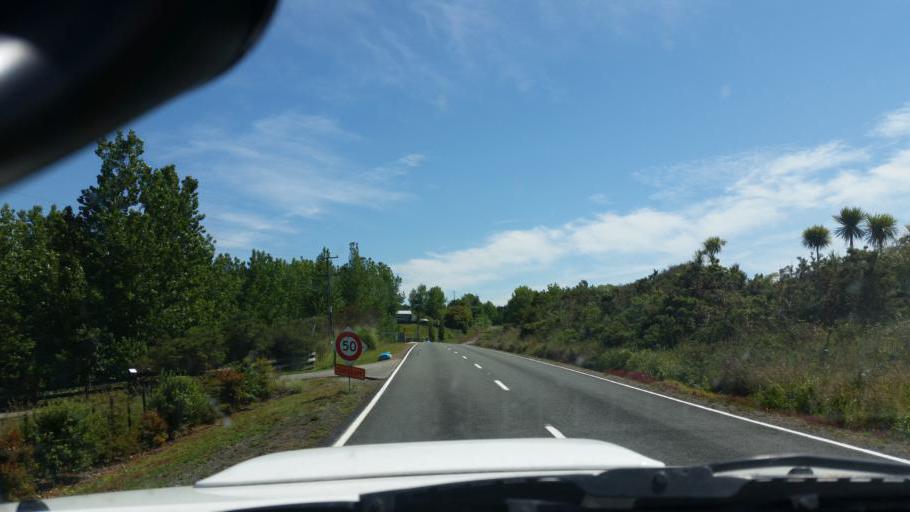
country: NZ
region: Auckland
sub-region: Auckland
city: Wellsford
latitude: -36.2154
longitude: 174.3898
